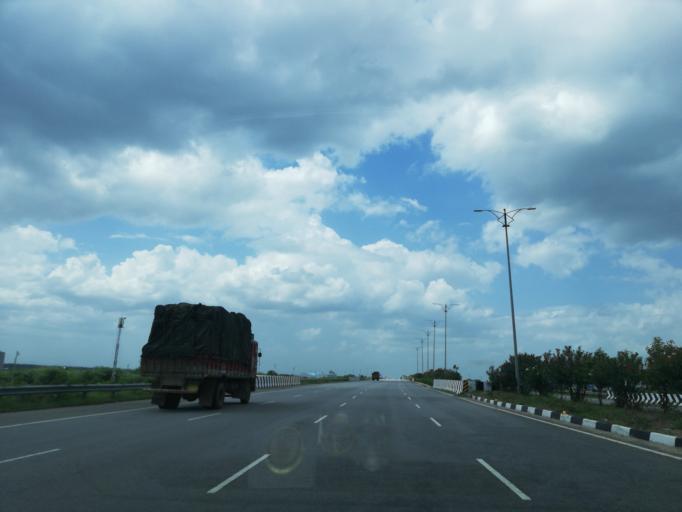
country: IN
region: Telangana
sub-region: Medak
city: Serilingampalle
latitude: 17.4622
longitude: 78.2497
